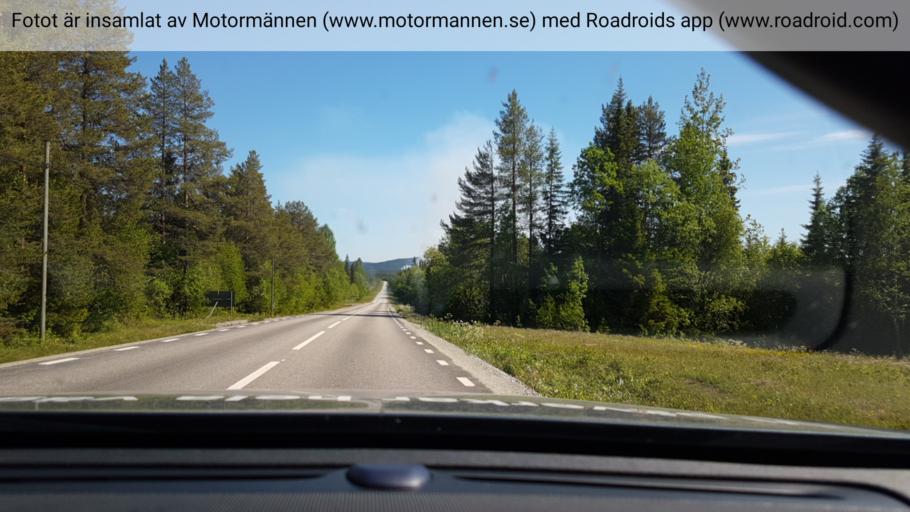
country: SE
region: Vaesterbotten
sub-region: Lycksele Kommun
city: Soderfors
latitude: 64.7090
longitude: 17.7134
